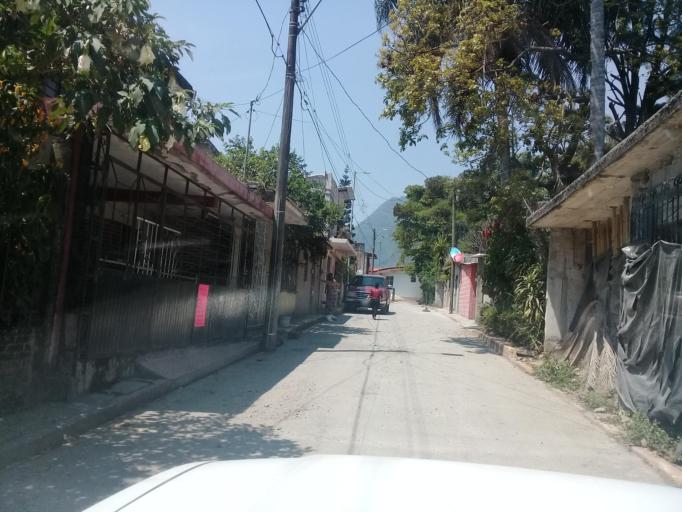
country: MX
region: Veracruz
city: Ixtac Zoquitlan
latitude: 18.8577
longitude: -97.0649
